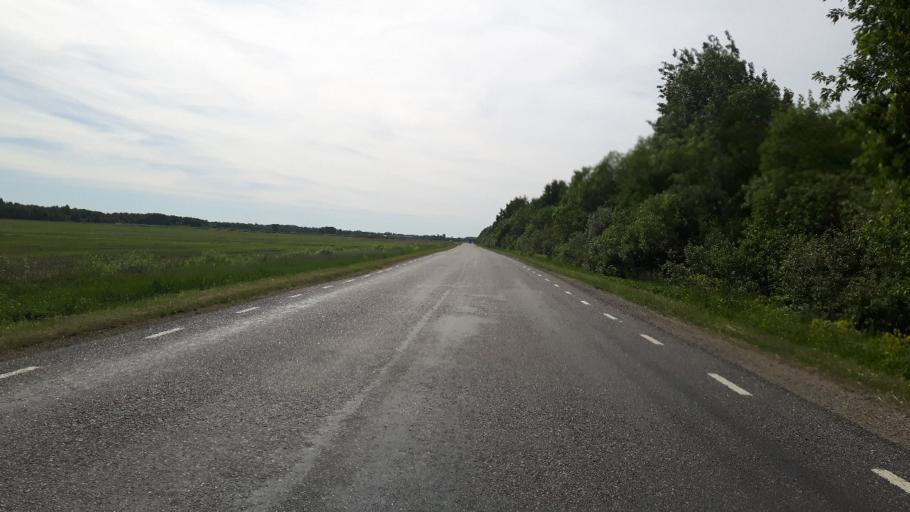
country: EE
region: Harju
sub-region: Raasiku vald
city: Arukula
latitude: 59.4263
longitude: 25.0696
